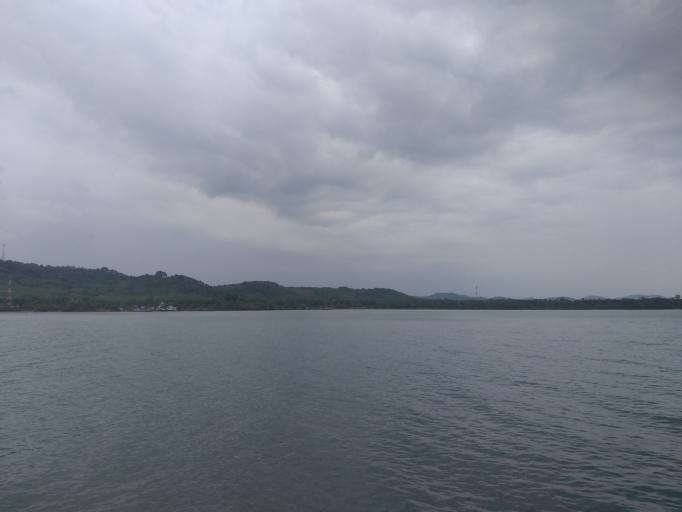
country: TH
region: Trat
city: Laem Ngop
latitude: 12.1768
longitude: 102.2999
